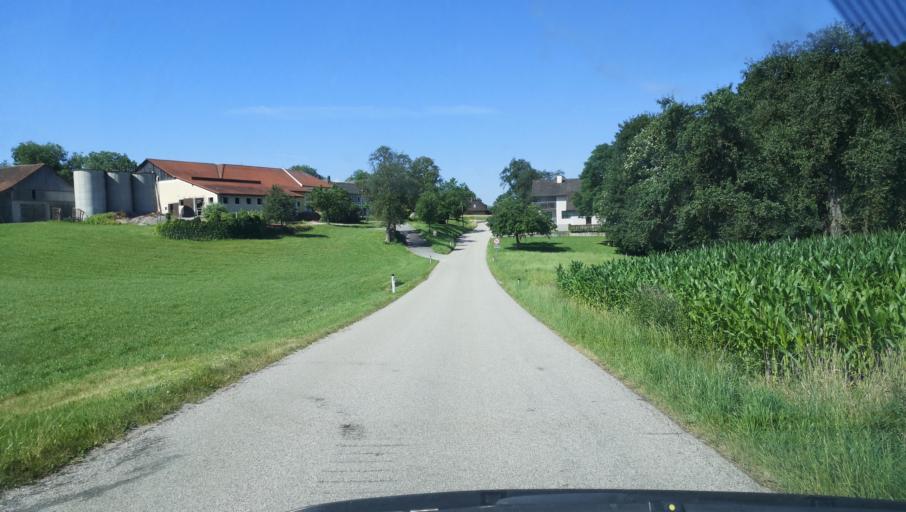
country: AT
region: Lower Austria
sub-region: Politischer Bezirk Amstetten
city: Euratsfeld
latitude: 48.0676
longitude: 14.9262
